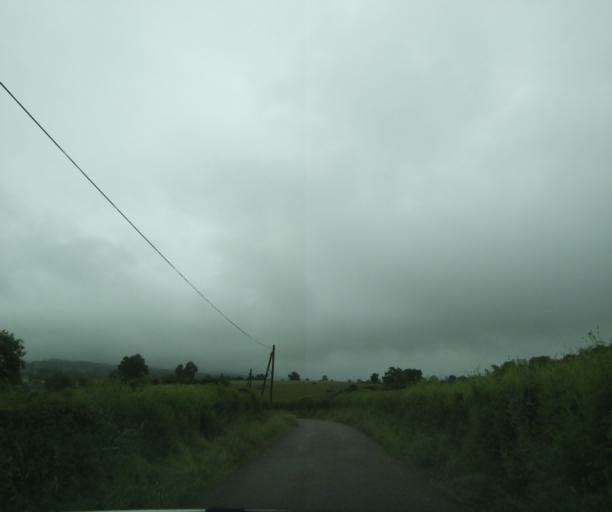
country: FR
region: Bourgogne
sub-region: Departement de Saone-et-Loire
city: Charolles
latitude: 46.3879
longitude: 4.3200
